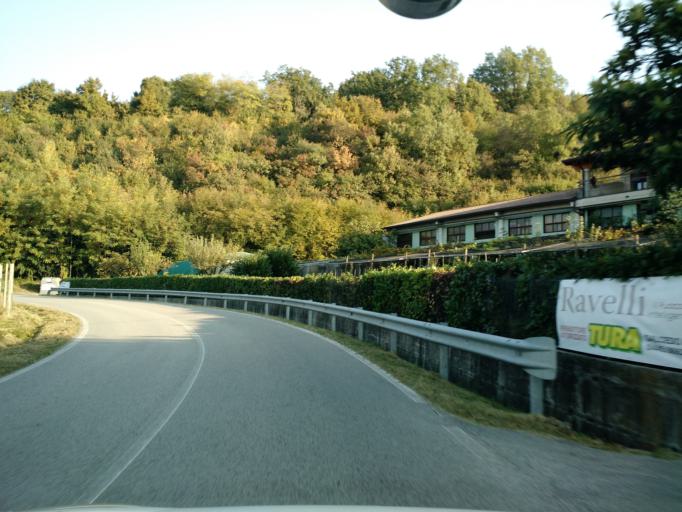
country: IT
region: Veneto
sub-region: Provincia di Vicenza
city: Salcedo
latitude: 45.7651
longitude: 11.5670
